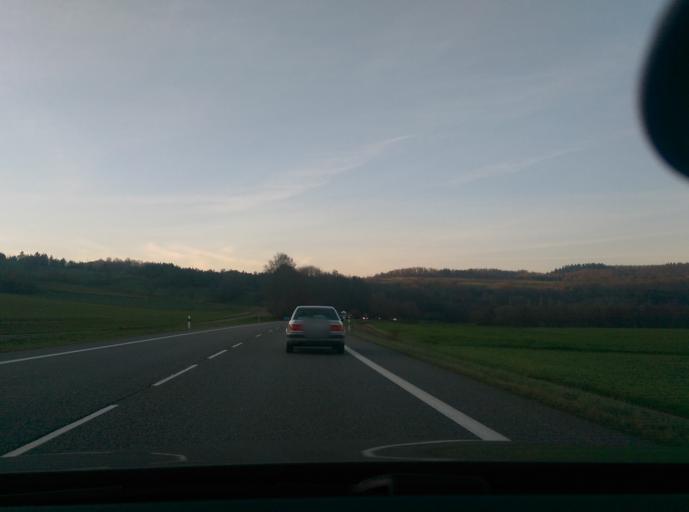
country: DE
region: Hesse
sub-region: Regierungsbezirk Kassel
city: Bad Sooden-Allendorf
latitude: 51.2135
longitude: 9.9902
